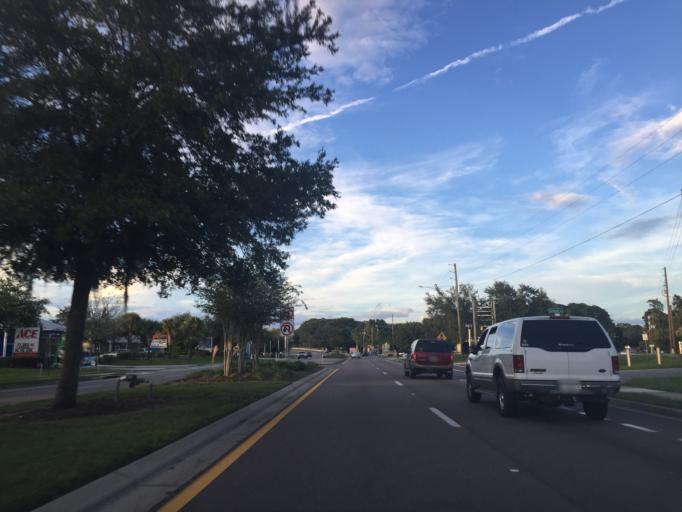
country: US
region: Florida
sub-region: Lake County
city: Tavares
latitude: 28.7966
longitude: -81.7412
